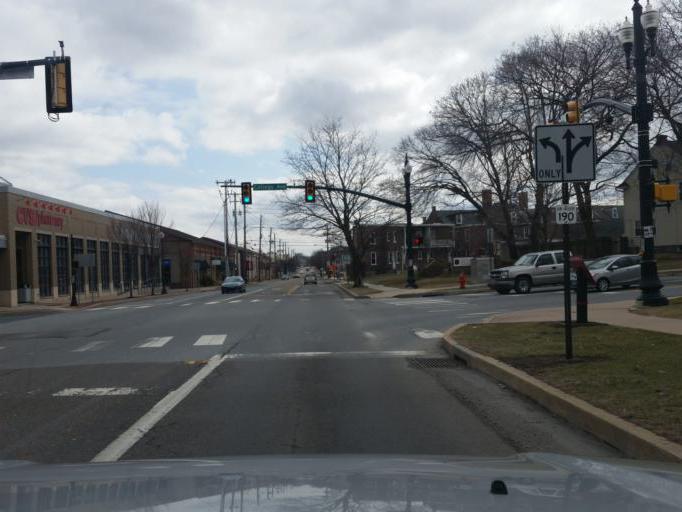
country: US
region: Pennsylvania
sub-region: Lancaster County
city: Lancaster
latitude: 40.0499
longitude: -76.3178
